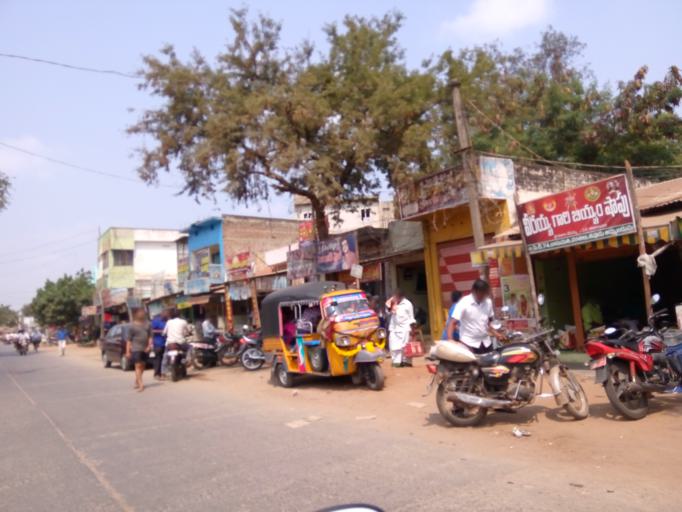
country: IN
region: Andhra Pradesh
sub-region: Prakasam
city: pedda nakkalapalem
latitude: 15.9668
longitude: 80.2773
